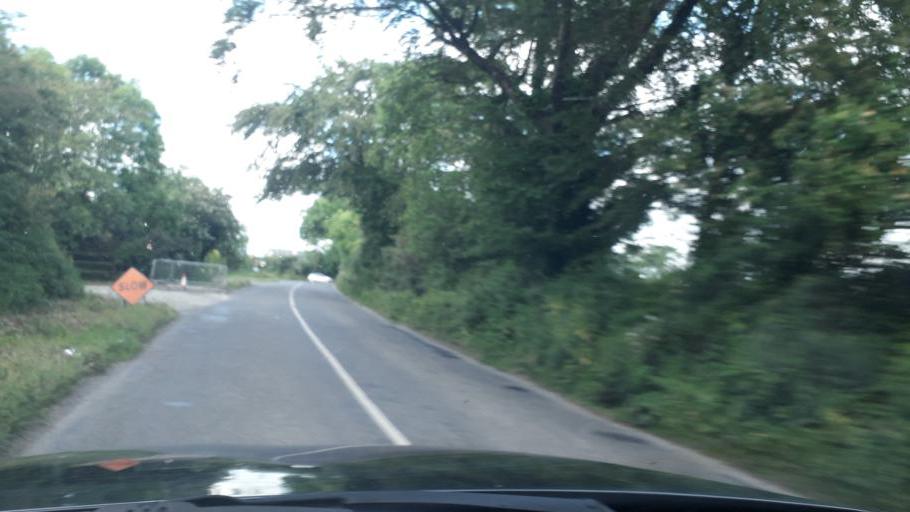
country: IE
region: Leinster
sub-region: Loch Garman
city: Loch Garman
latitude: 52.2835
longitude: -6.5369
